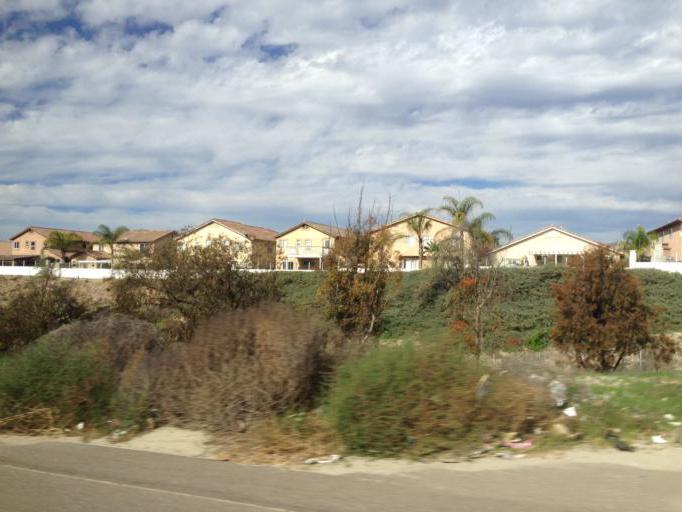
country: MX
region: Baja California
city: Tijuana
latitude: 32.5685
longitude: -117.0353
